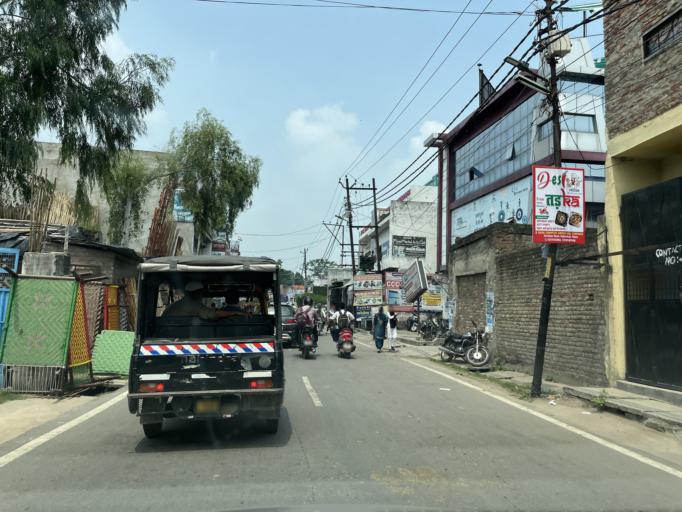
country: IN
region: Uttar Pradesh
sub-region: Bijnor
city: Najibabad
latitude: 29.6067
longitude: 78.3372
